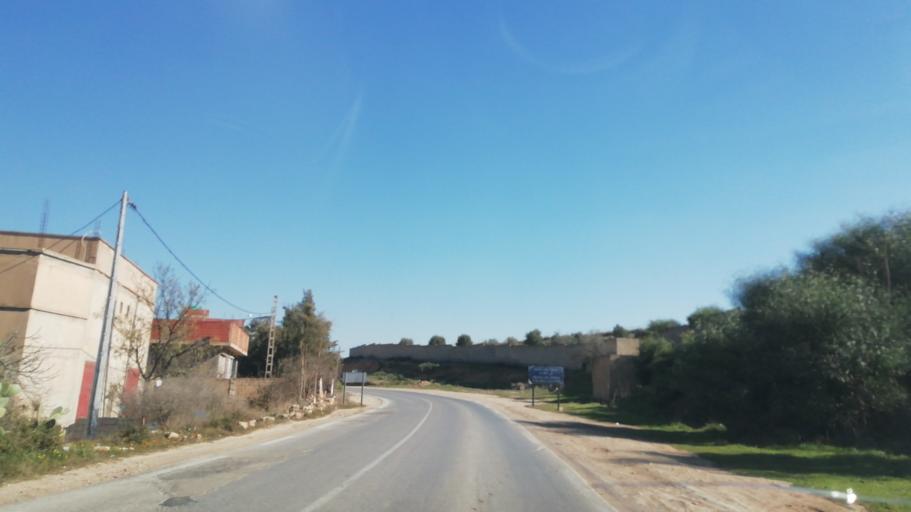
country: DZ
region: Tlemcen
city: Nedroma
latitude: 34.8402
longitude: -1.7084
